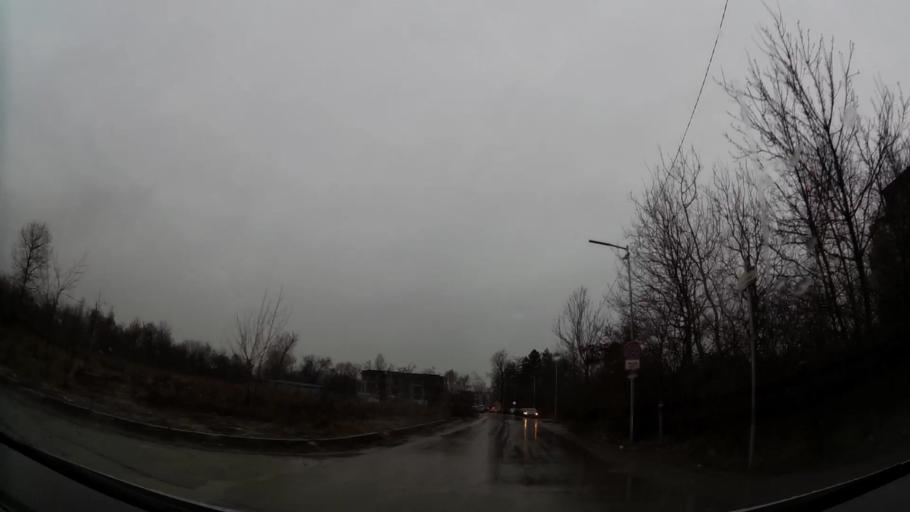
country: BG
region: Sofia-Capital
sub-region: Stolichna Obshtina
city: Sofia
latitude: 42.6525
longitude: 23.3201
